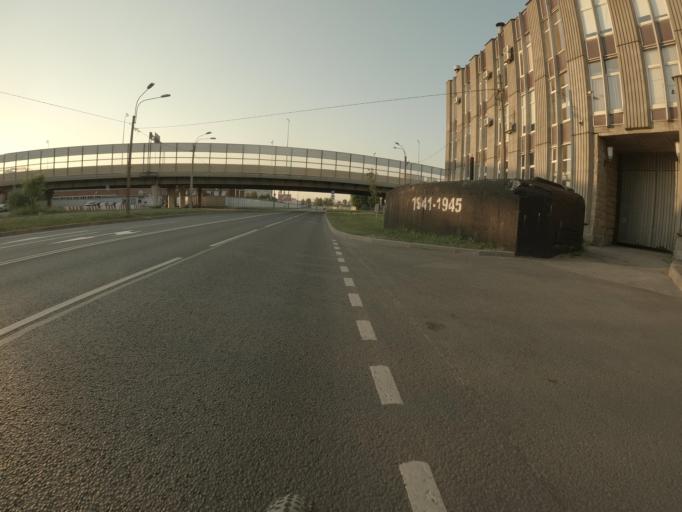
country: RU
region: St.-Petersburg
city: Avtovo
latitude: 59.8550
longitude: 30.2817
